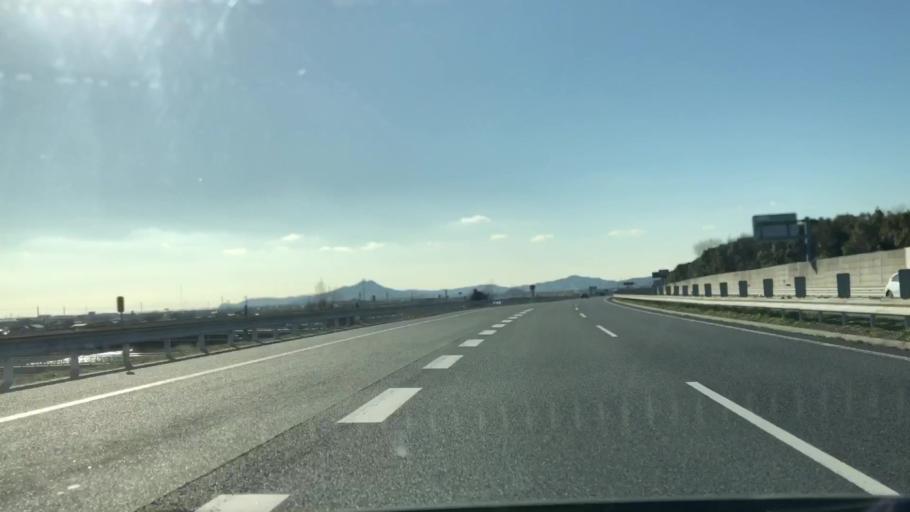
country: JP
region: Yamaguchi
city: Hofu
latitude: 34.0552
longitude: 131.5370
